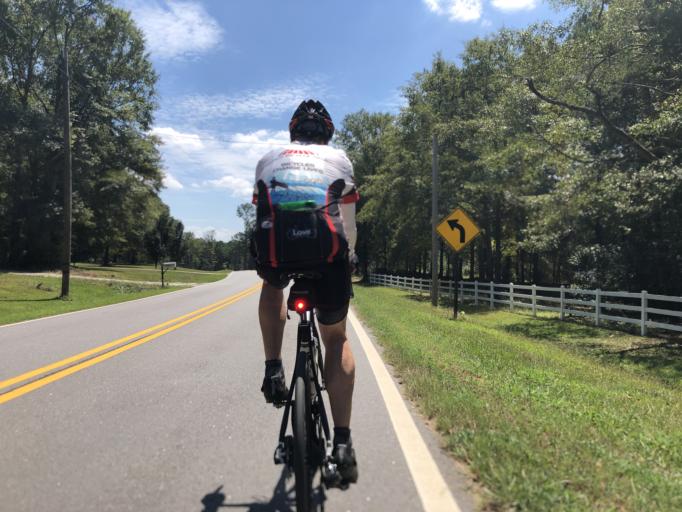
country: US
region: Georgia
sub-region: Fulton County
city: Chattahoochee Hills
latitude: 33.4896
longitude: -84.8166
